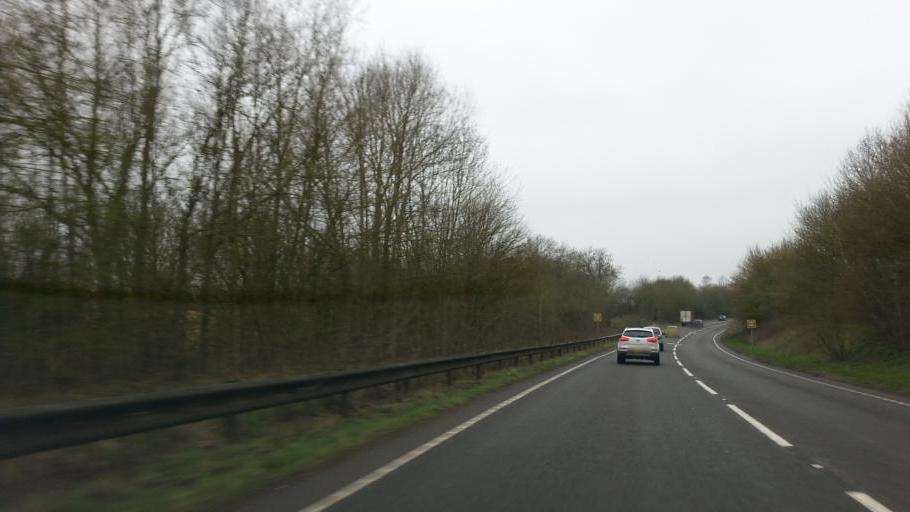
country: GB
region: England
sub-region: Oxfordshire
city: Adderbury
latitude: 52.0693
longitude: -1.2784
